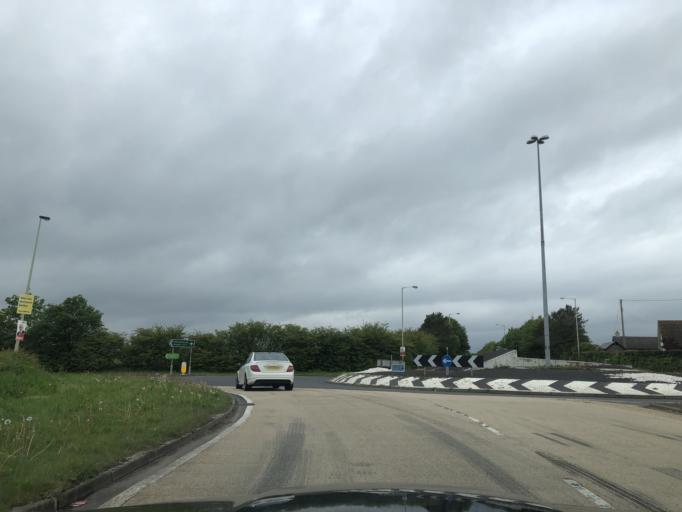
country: GB
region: Northern Ireland
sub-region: Antrim Borough
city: Antrim
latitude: 54.6694
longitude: -6.1793
